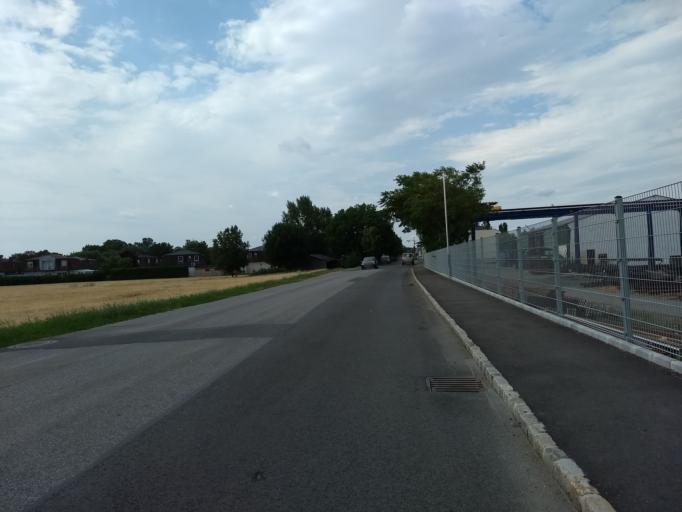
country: AT
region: Lower Austria
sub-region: Politischer Bezirk Modling
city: Guntramsdorf
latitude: 48.0538
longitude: 16.3224
